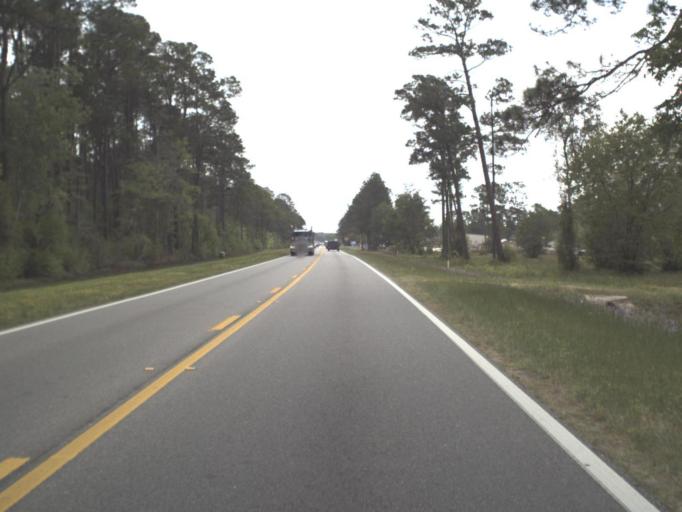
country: US
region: Florida
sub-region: Escambia County
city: Myrtle Grove
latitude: 30.3562
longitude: -87.3696
